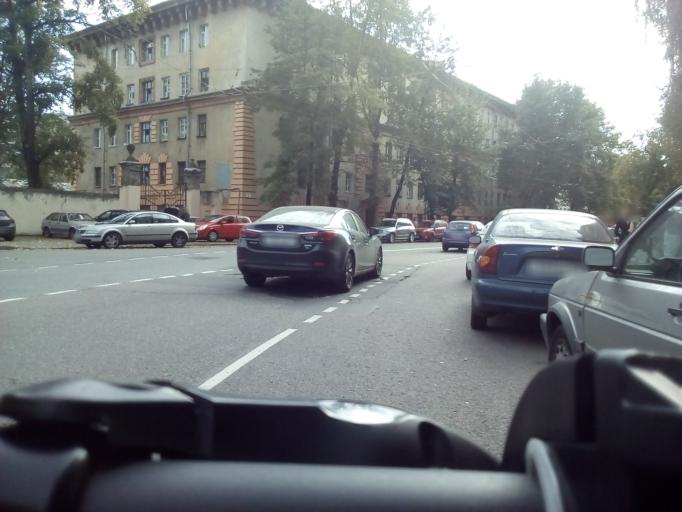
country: RU
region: Moscow
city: Lefortovo
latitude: 55.7872
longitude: 37.7058
